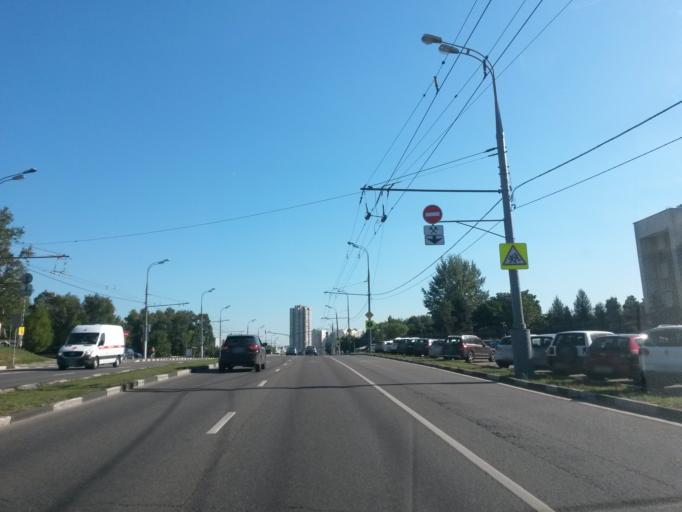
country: RU
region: Moscow
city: Yasenevo
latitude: 55.6265
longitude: 37.5412
